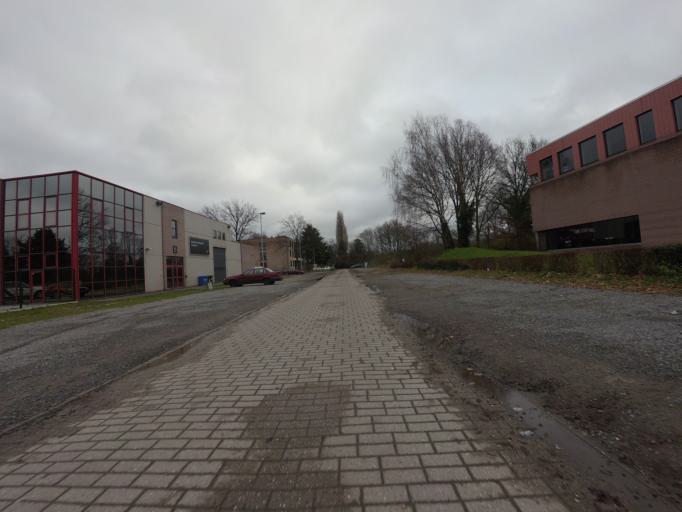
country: BE
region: Flanders
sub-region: Provincie Antwerpen
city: Hoboken
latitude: 51.1736
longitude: 4.3718
